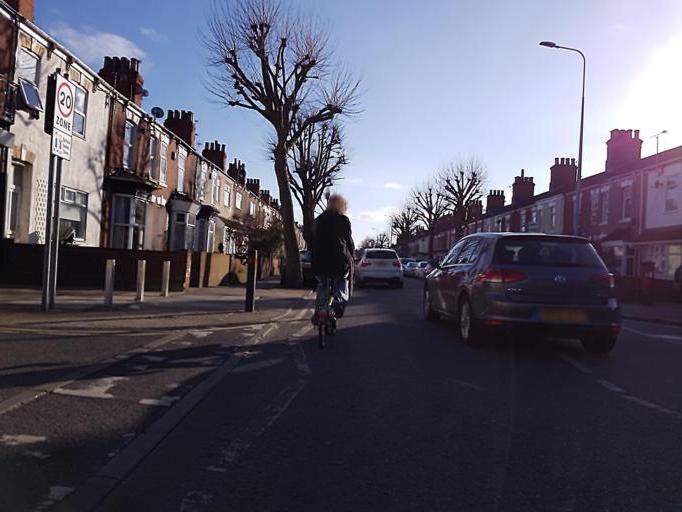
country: GB
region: England
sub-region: North East Lincolnshire
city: Grimsby
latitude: 53.5623
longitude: -0.0760
